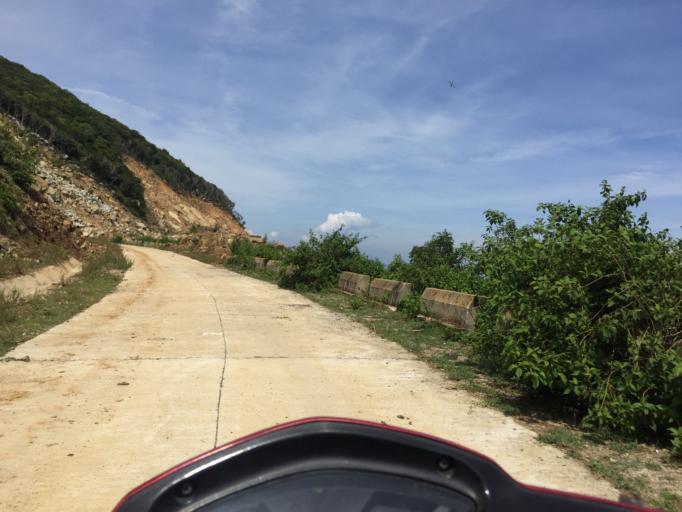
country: VN
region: Quang Nam
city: Hoi An
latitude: 15.9743
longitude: 108.5072
